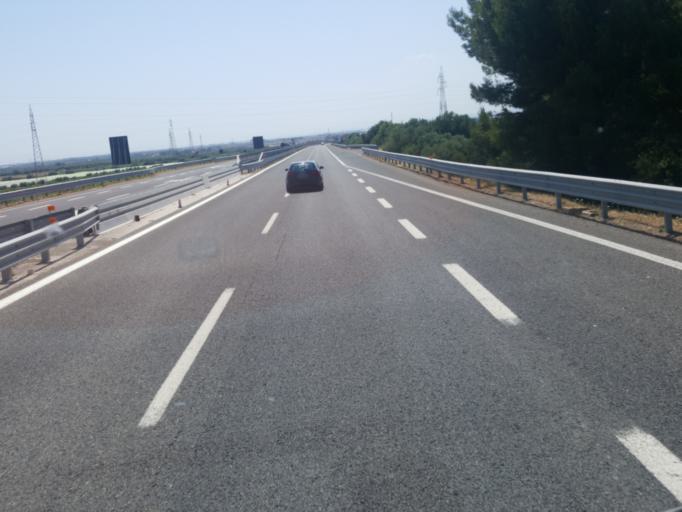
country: IT
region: Apulia
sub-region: Provincia di Taranto
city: Massafra
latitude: 40.5958
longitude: 17.0785
